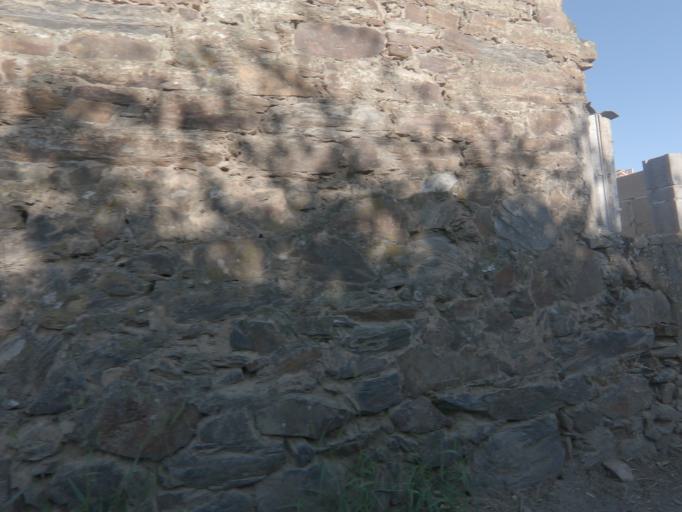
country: PT
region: Vila Real
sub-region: Peso da Regua
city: Peso da Regua
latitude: 41.1692
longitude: -7.7814
